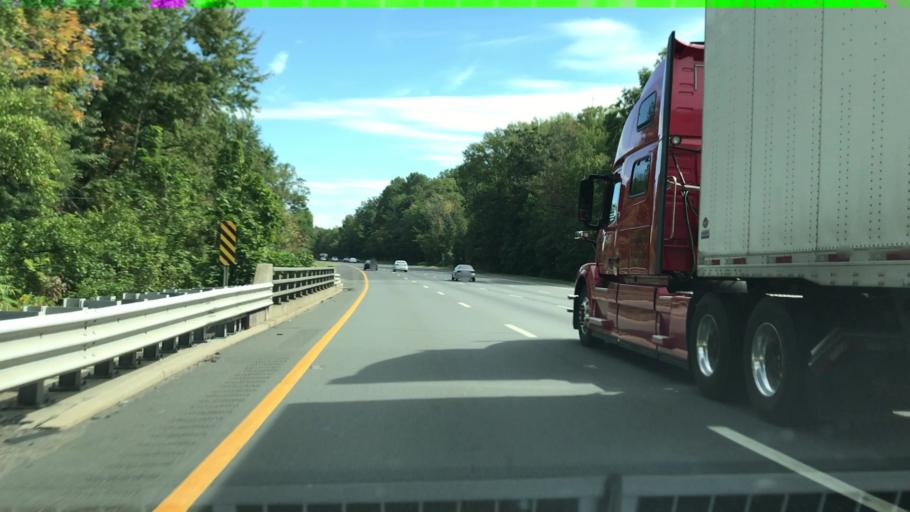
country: US
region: New Jersey
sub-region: Burlington County
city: Roebling
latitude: 40.0638
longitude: -74.7988
